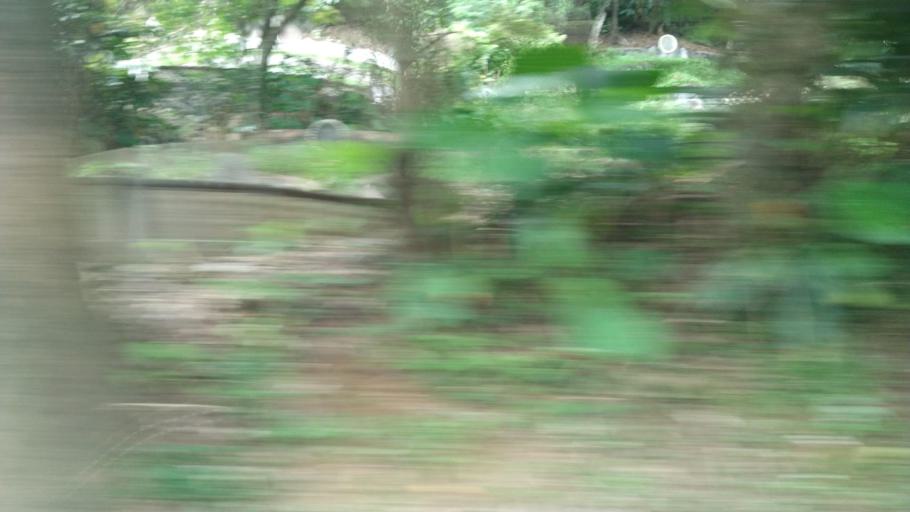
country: TW
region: Taiwan
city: Daxi
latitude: 24.9124
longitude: 121.3746
